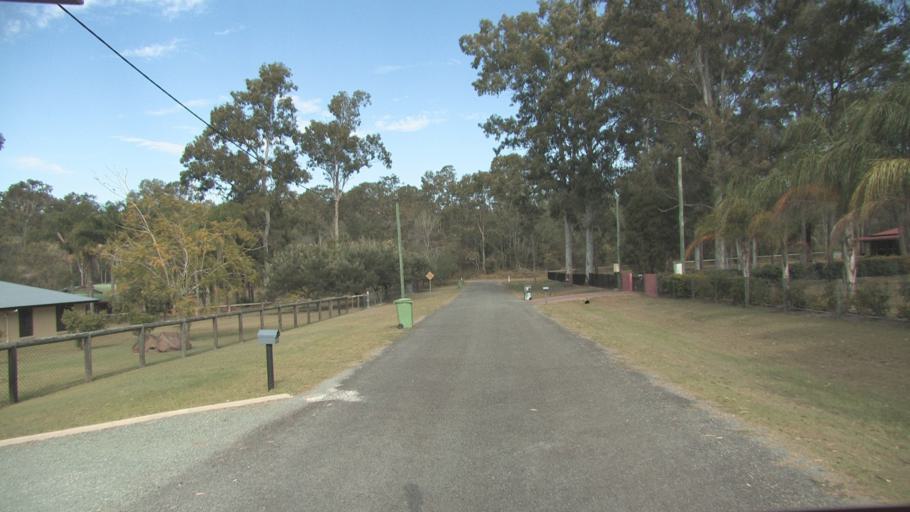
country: AU
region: Queensland
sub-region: Logan
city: North Maclean
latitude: -27.7673
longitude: 152.9904
